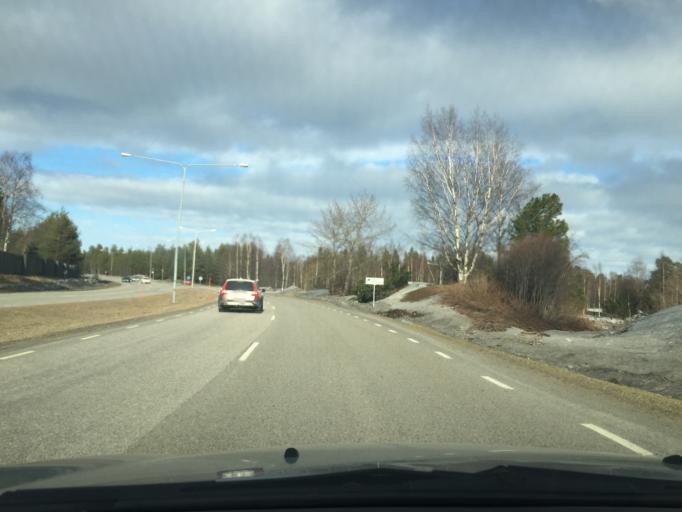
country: SE
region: Norrbotten
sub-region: Lulea Kommun
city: Lulea
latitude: 65.5850
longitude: 22.2188
